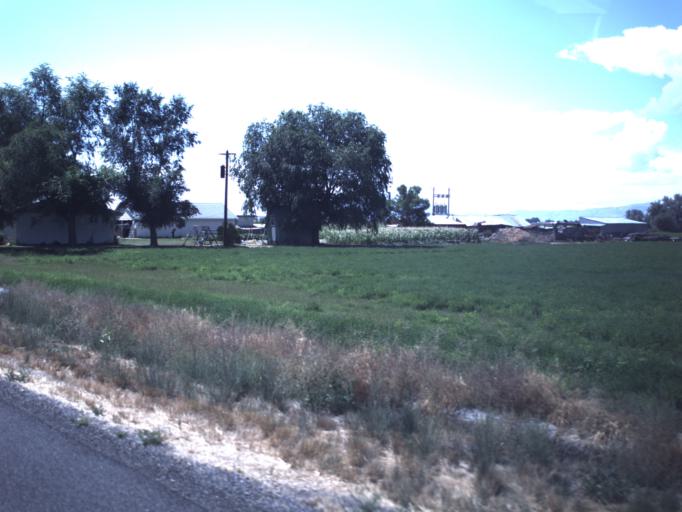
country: US
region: Utah
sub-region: Box Elder County
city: Honeyville
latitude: 41.5808
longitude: -112.1298
